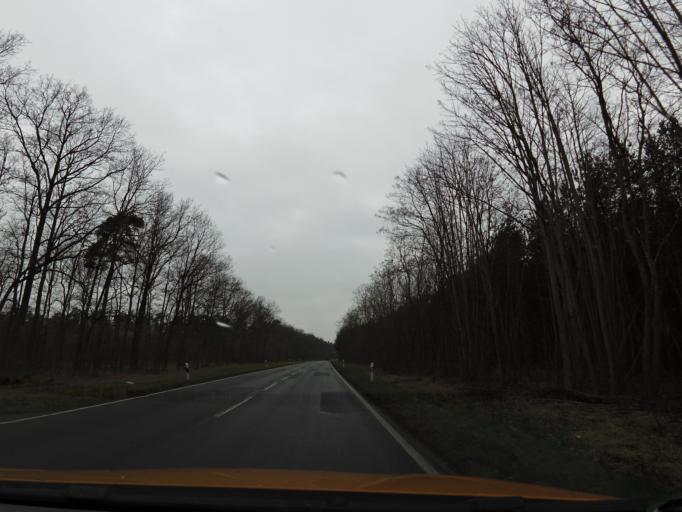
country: DE
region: Brandenburg
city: Gross Kreutz
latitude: 52.4045
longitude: 12.7588
